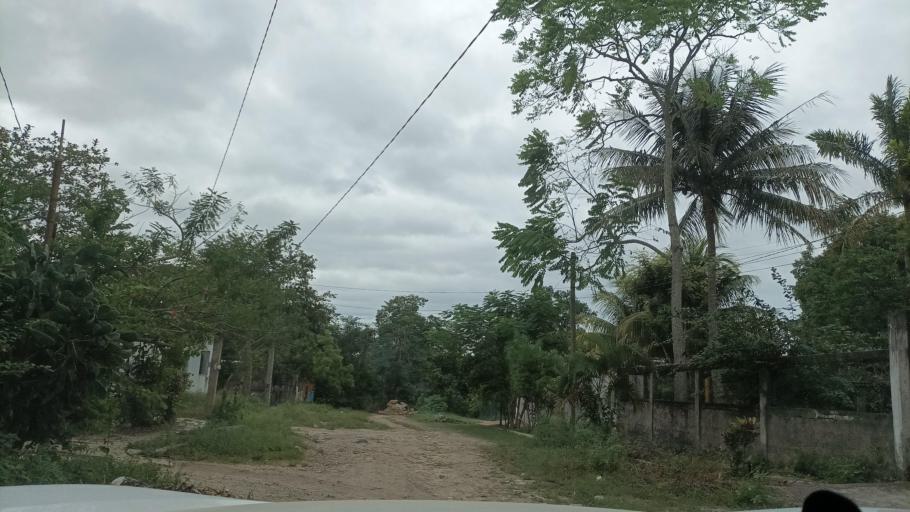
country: MX
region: Veracruz
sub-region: Cosoleacaque
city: Coacotla
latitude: 17.9532
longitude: -94.7163
